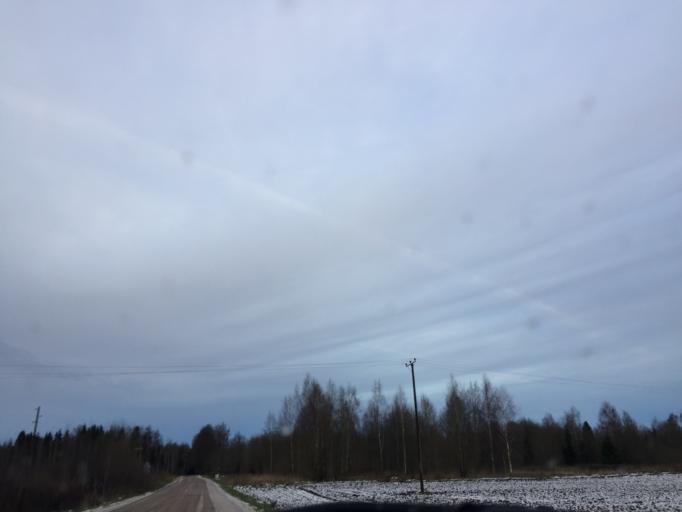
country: LV
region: Limbazu Rajons
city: Limbazi
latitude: 57.5536
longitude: 24.8157
